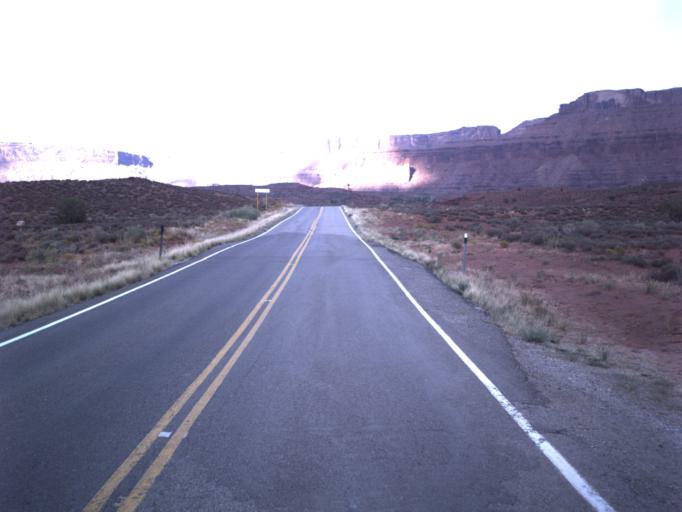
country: US
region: Utah
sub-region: Grand County
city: Moab
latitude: 38.7245
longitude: -109.3550
